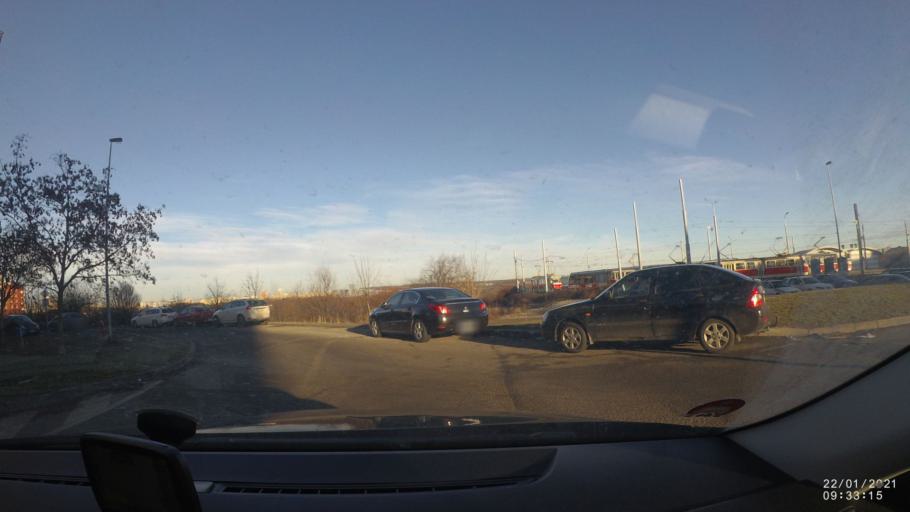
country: CZ
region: Praha
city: Branik
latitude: 50.0310
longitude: 14.3664
